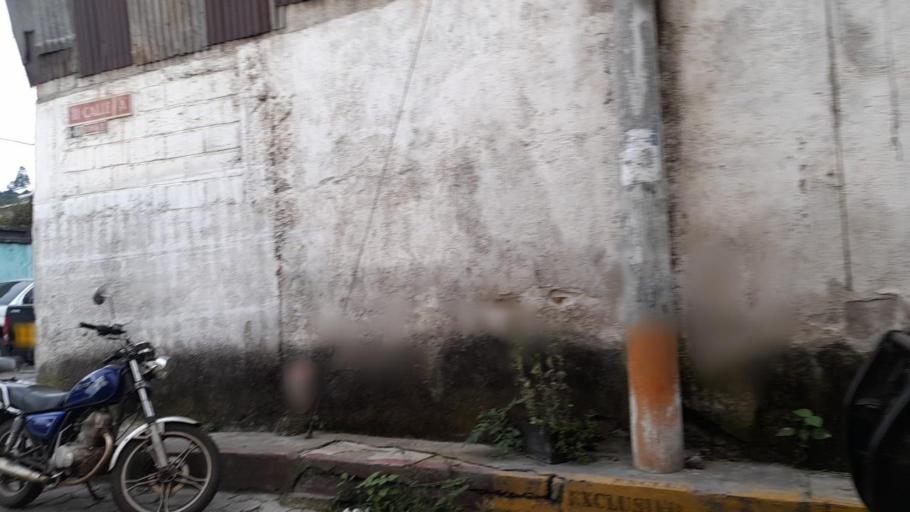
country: GT
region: Quetzaltenango
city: Quetzaltenango
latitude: 14.8293
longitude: -91.5142
